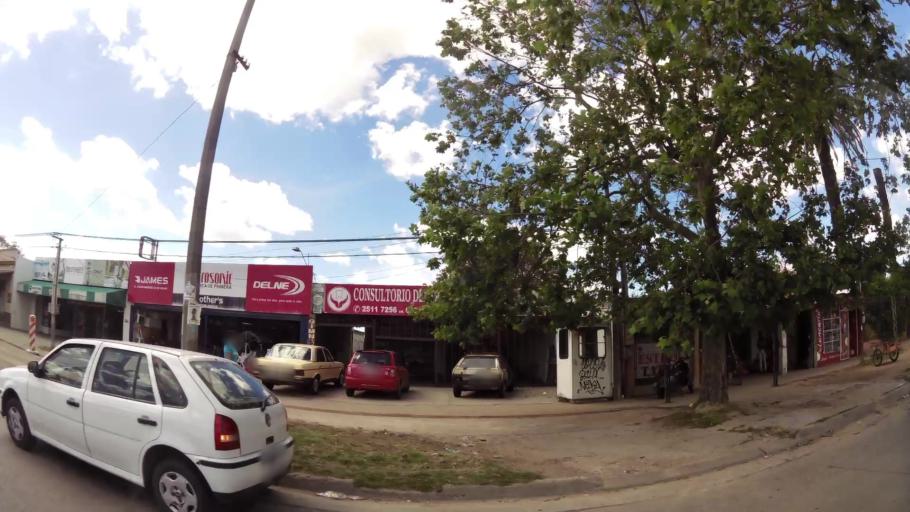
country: UY
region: Canelones
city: Paso de Carrasco
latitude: -34.8366
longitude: -56.1157
